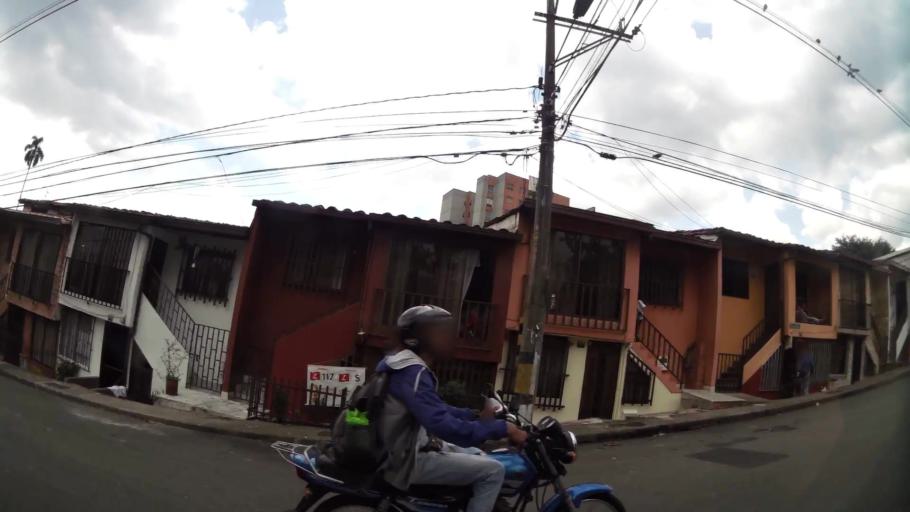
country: CO
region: Antioquia
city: Envigado
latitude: 6.1614
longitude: -75.5921
